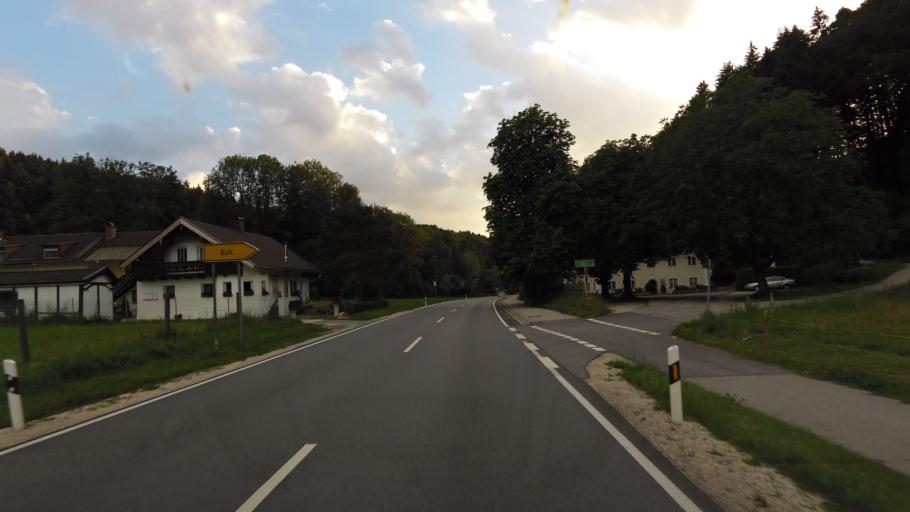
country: DE
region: Bavaria
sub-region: Upper Bavaria
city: Surberg
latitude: 47.8616
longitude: 12.6925
